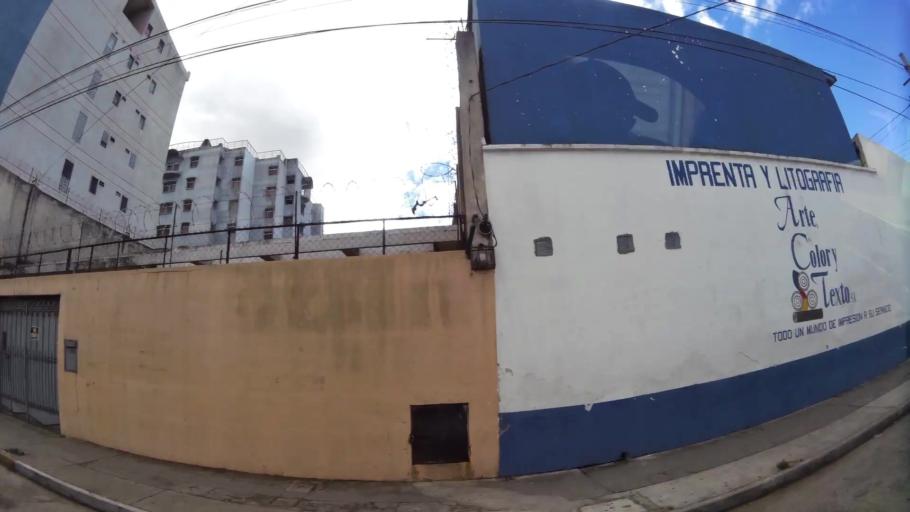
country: GT
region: Guatemala
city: Guatemala City
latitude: 14.6112
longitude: -90.5110
